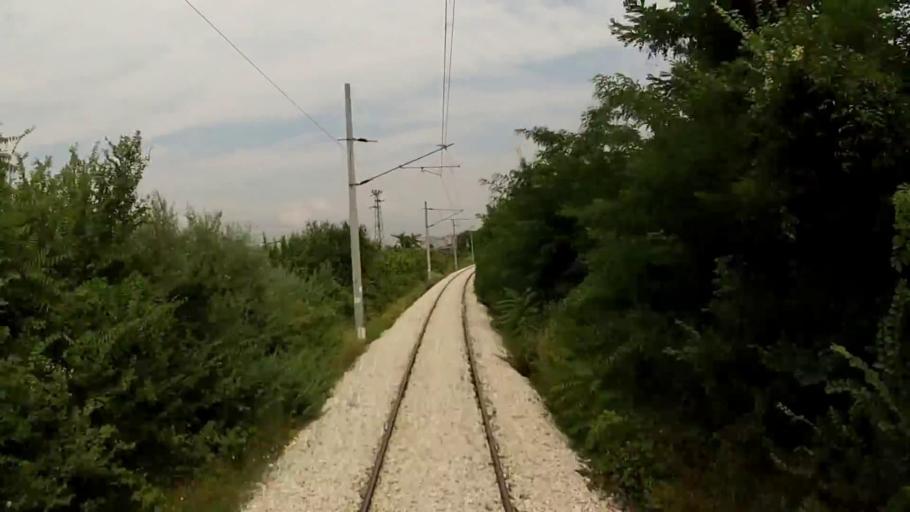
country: BG
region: Blagoevgrad
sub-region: Obshtina Blagoevgrad
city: Blagoevgrad
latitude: 41.9713
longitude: 23.0956
